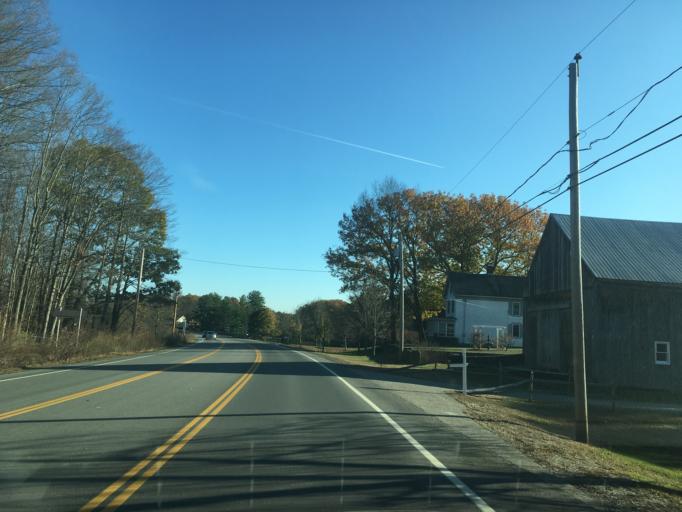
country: US
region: New Hampshire
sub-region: Rockingham County
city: Stratham Station
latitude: 43.0413
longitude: -70.9301
